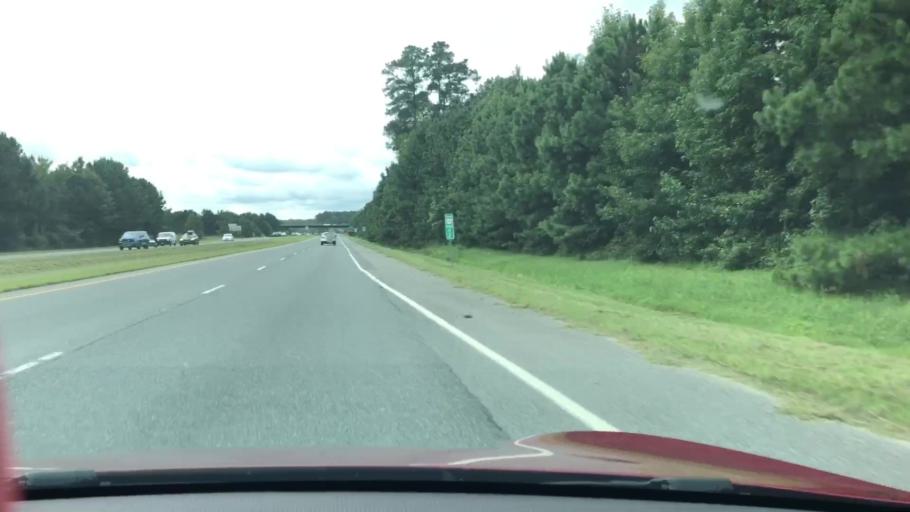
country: US
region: Virginia
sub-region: City of Chesapeake
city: Chesapeake
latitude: 36.6794
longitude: -76.2301
